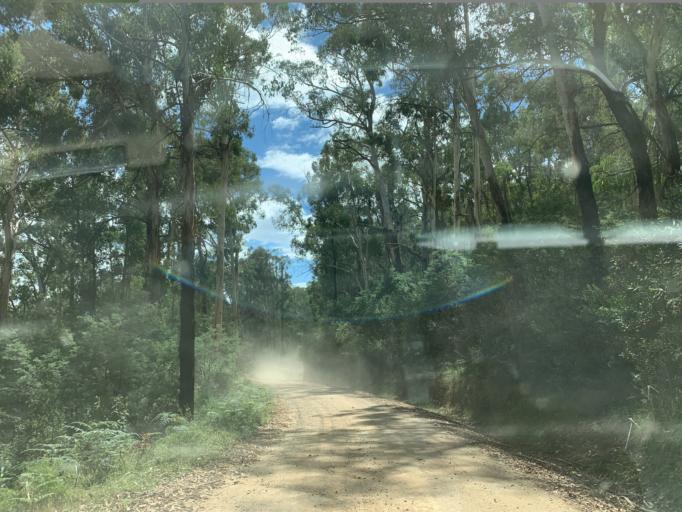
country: AU
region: Victoria
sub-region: Mansfield
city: Mansfield
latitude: -37.0950
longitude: 146.5158
